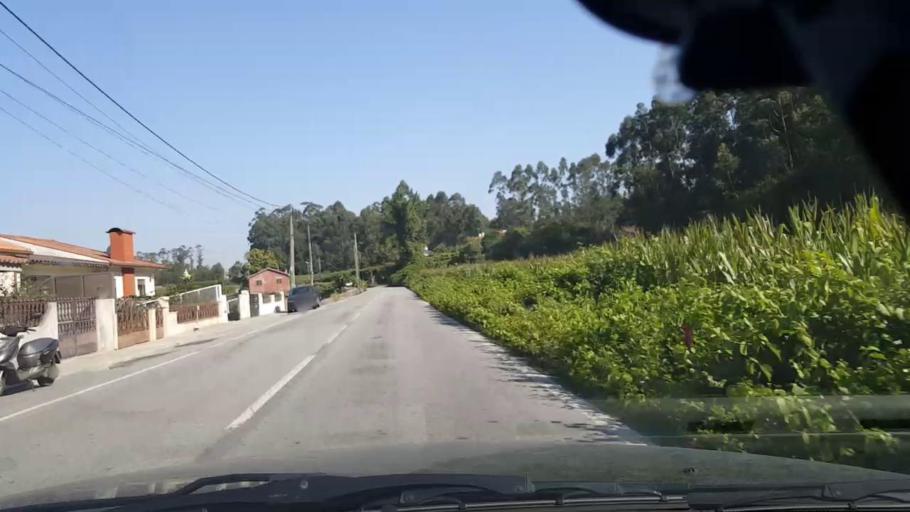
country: PT
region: Porto
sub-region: Vila do Conde
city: Arvore
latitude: 41.3140
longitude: -8.6791
